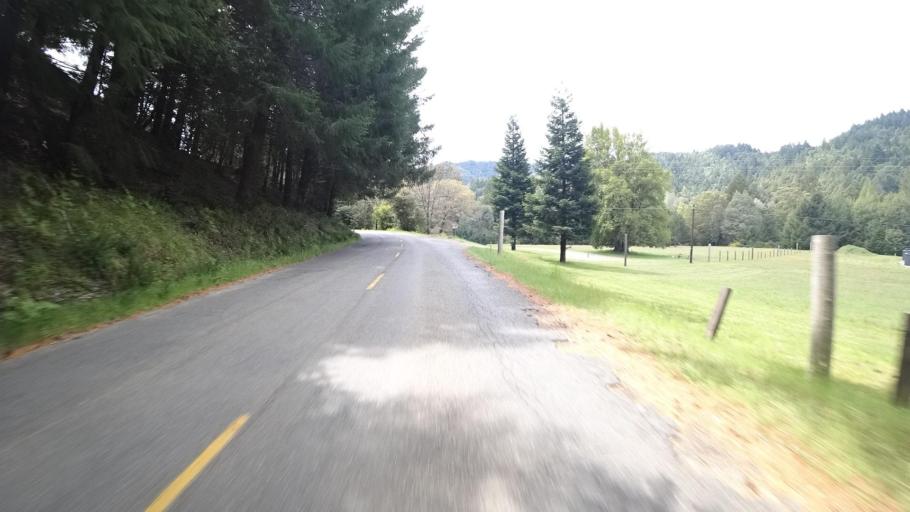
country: US
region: California
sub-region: Humboldt County
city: Redway
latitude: 40.0477
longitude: -123.9610
